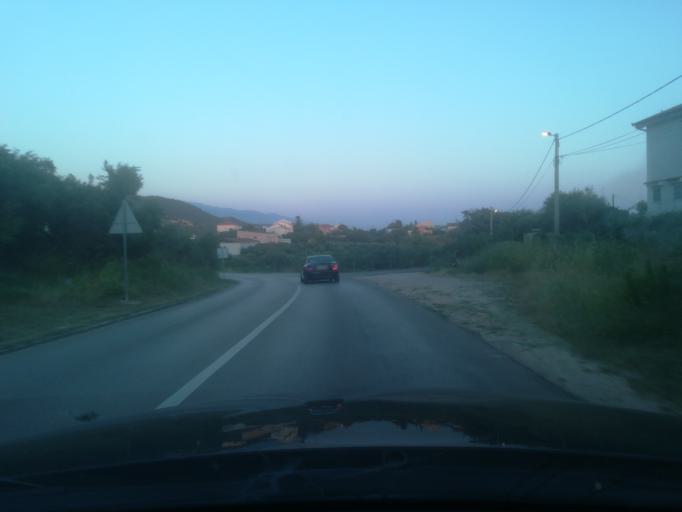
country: HR
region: Primorsko-Goranska
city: Banjol
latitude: 44.7532
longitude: 14.7794
